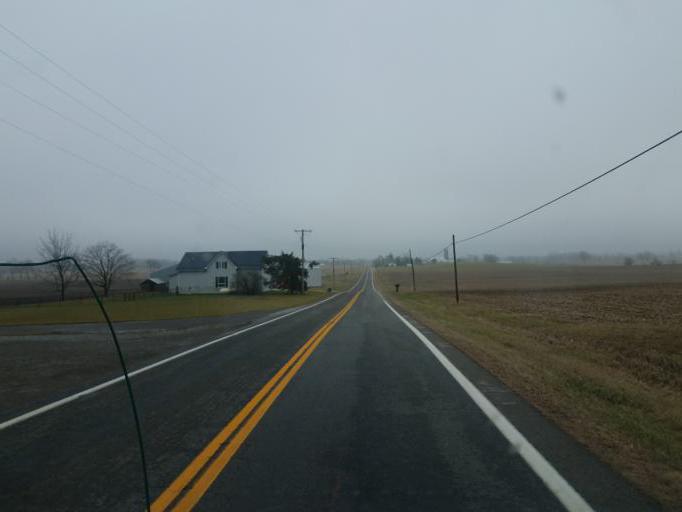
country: US
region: Ohio
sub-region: Champaign County
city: North Lewisburg
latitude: 40.2424
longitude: -83.5703
